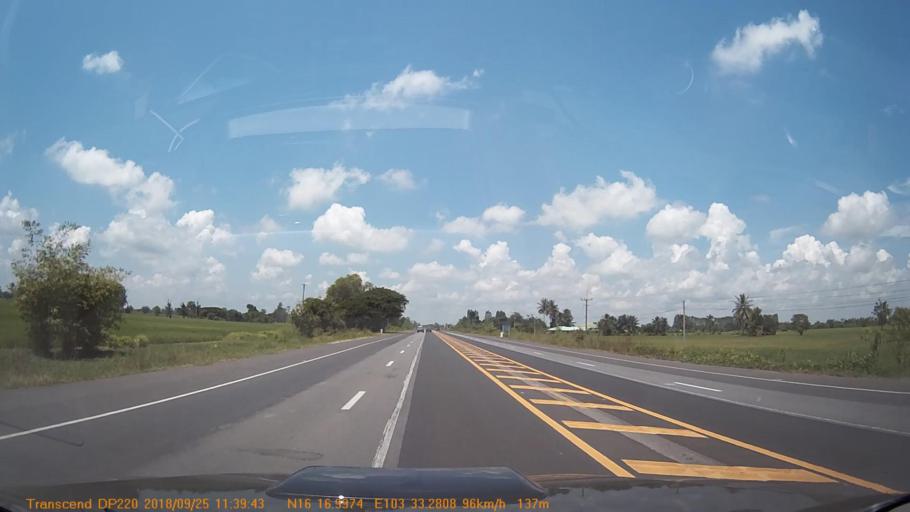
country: TH
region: Kalasin
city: Kamalasai
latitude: 16.2830
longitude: 103.5545
